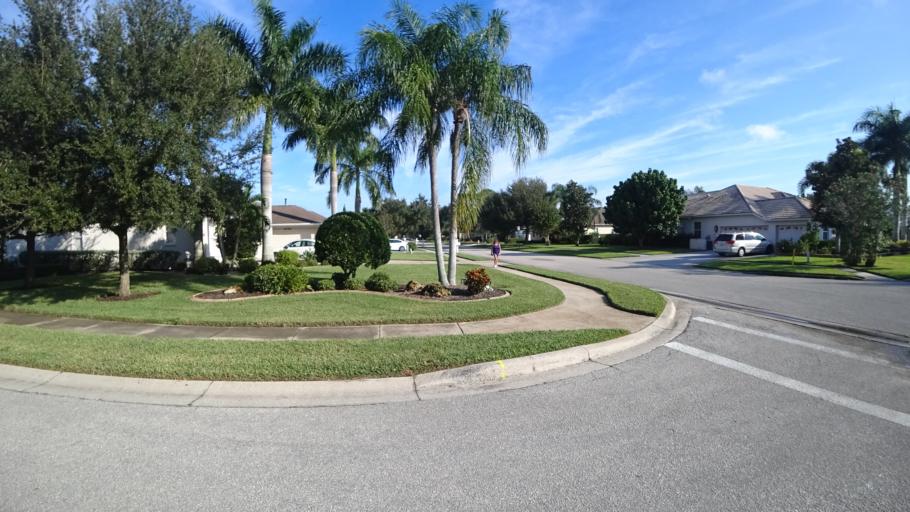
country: US
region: Florida
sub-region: Sarasota County
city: Desoto Lakes
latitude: 27.4197
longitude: -82.4958
